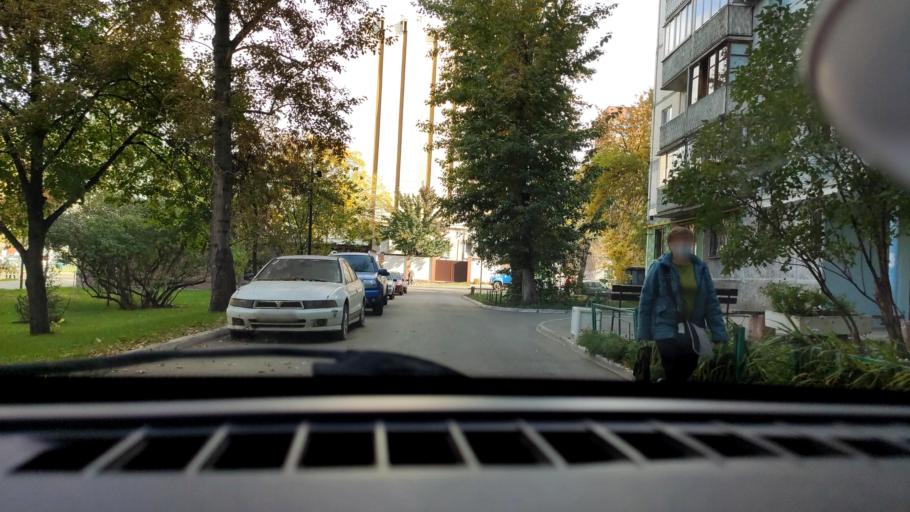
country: RU
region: Samara
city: Samara
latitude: 53.2008
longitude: 50.1353
